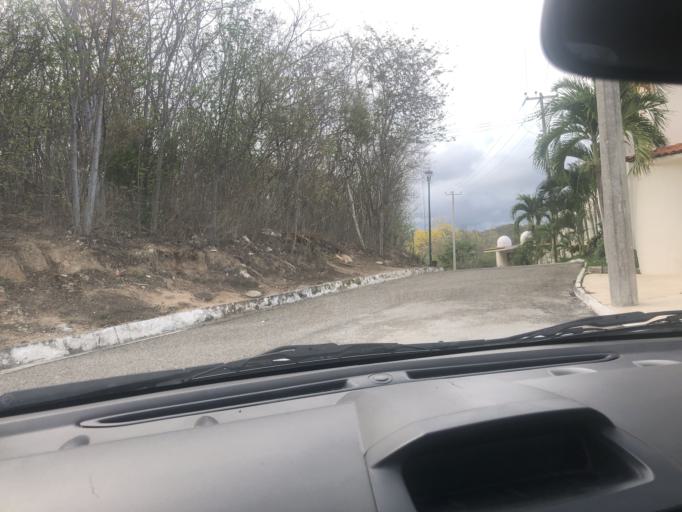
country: MX
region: Oaxaca
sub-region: Santa Maria Huatulco
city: Crucecita
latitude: 15.7717
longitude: -96.0865
